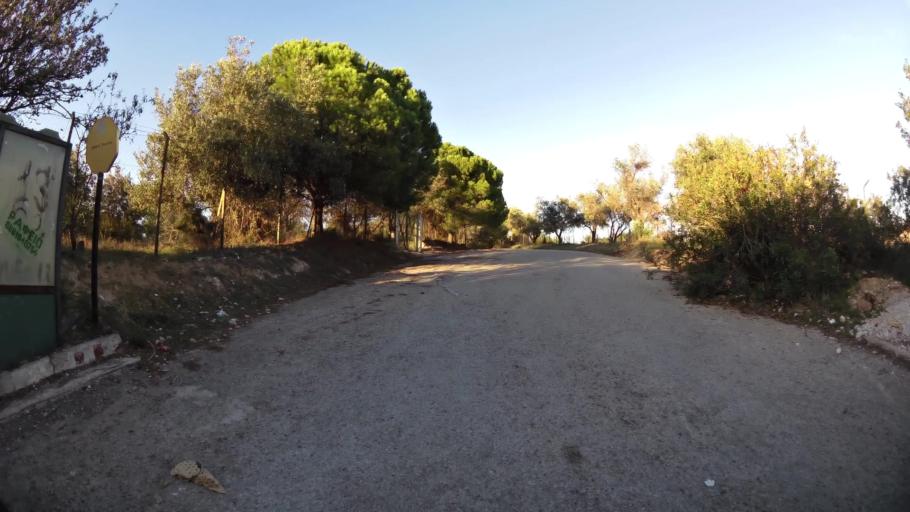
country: GR
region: Attica
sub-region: Nomarchia Anatolikis Attikis
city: Spata
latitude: 37.9669
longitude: 23.9184
